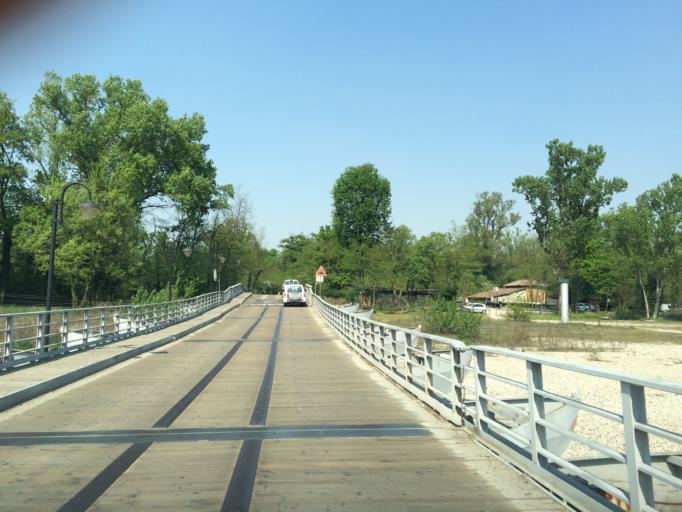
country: IT
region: Lombardy
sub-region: Provincia di Pavia
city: Bereguardo
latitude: 45.2354
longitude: 9.0077
